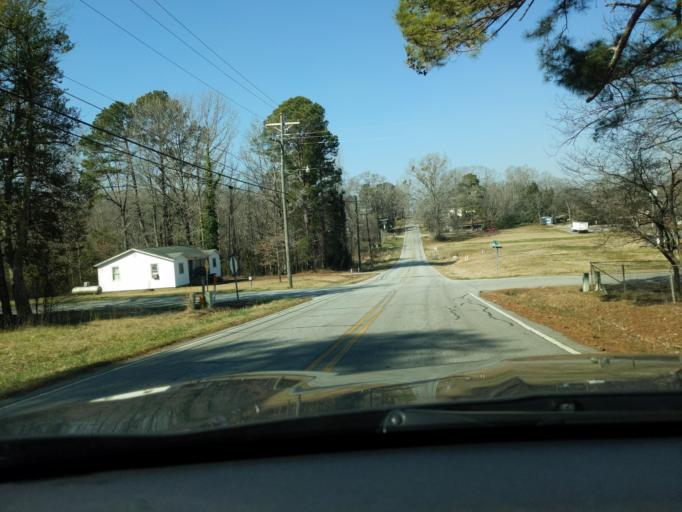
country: US
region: South Carolina
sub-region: Abbeville County
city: Calhoun Falls
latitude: 34.0896
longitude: -82.5923
